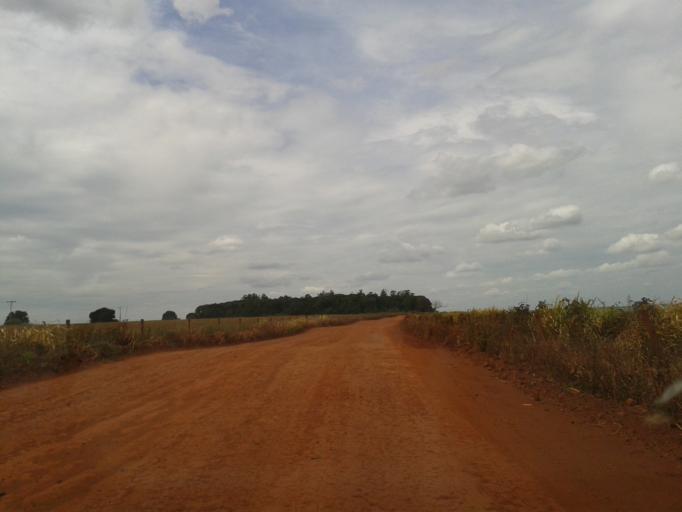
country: BR
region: Minas Gerais
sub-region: Centralina
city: Centralina
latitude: -18.7657
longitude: -49.2384
